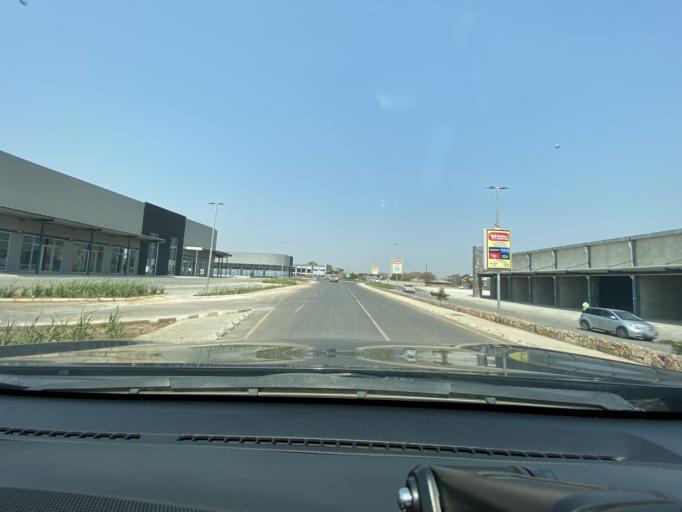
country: ZM
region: Lusaka
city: Lusaka
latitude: -15.3920
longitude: 28.3225
